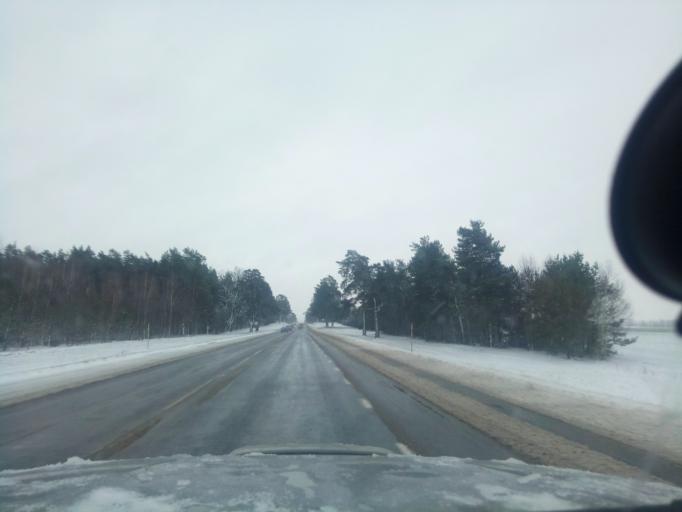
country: BY
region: Minsk
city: Nyasvizh
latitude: 53.2554
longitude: 26.6160
